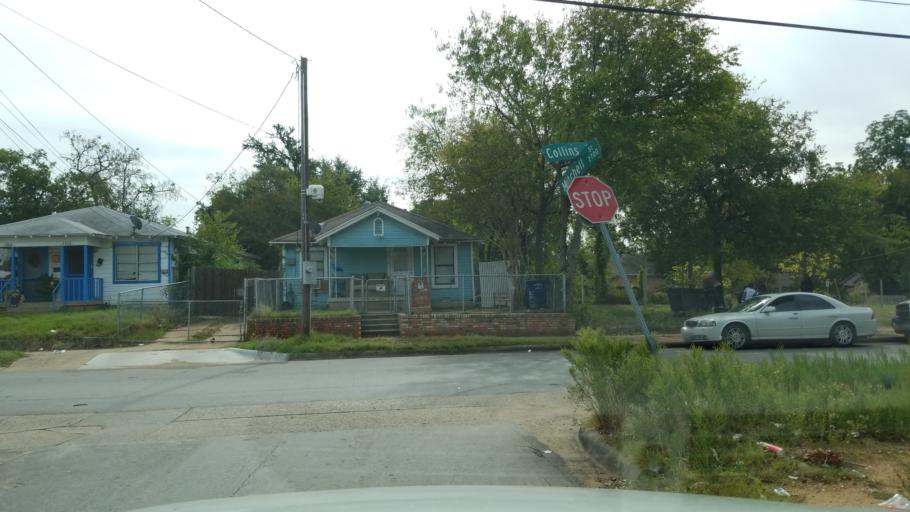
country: US
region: Texas
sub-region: Dallas County
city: Dallas
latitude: 32.7766
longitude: -96.7423
